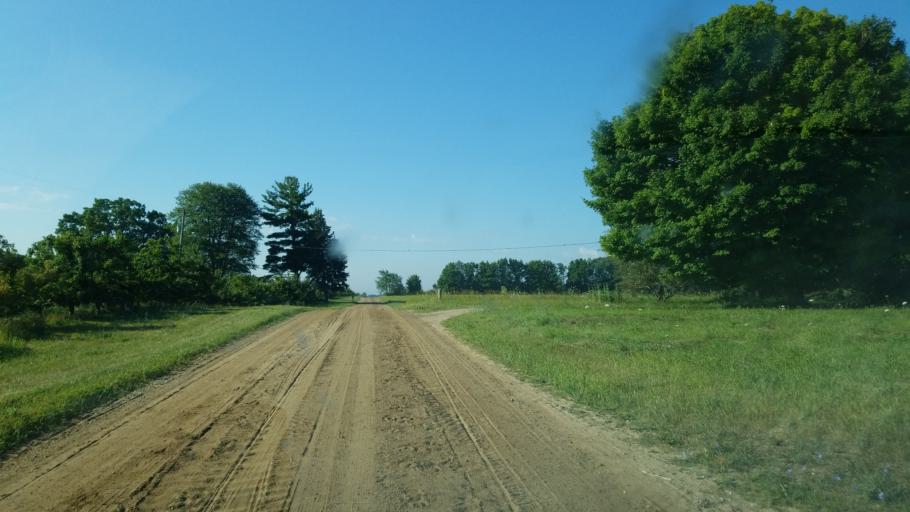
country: US
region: Michigan
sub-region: Mecosta County
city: Canadian Lakes
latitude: 43.5648
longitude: -85.3538
